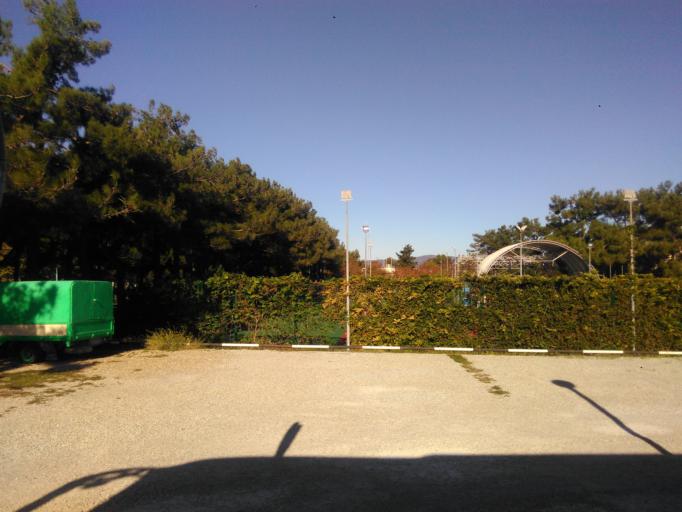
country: RU
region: Krasnodarskiy
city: Gelendzhik
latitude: 44.5497
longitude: 38.0540
